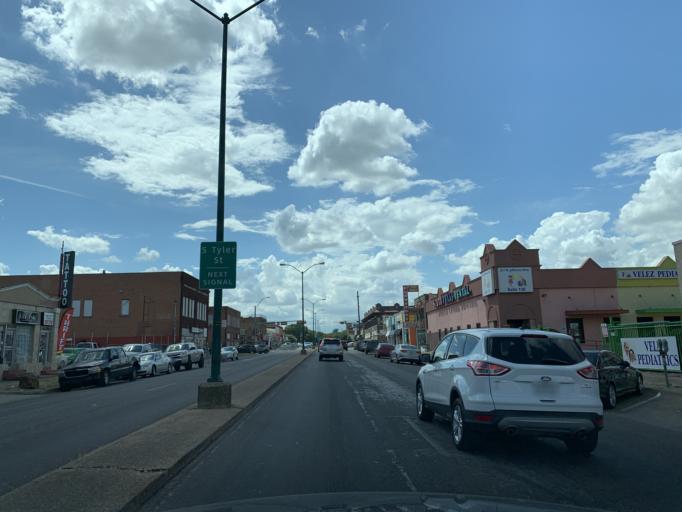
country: US
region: Texas
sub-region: Dallas County
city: Dallas
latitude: 32.7432
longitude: -96.8363
